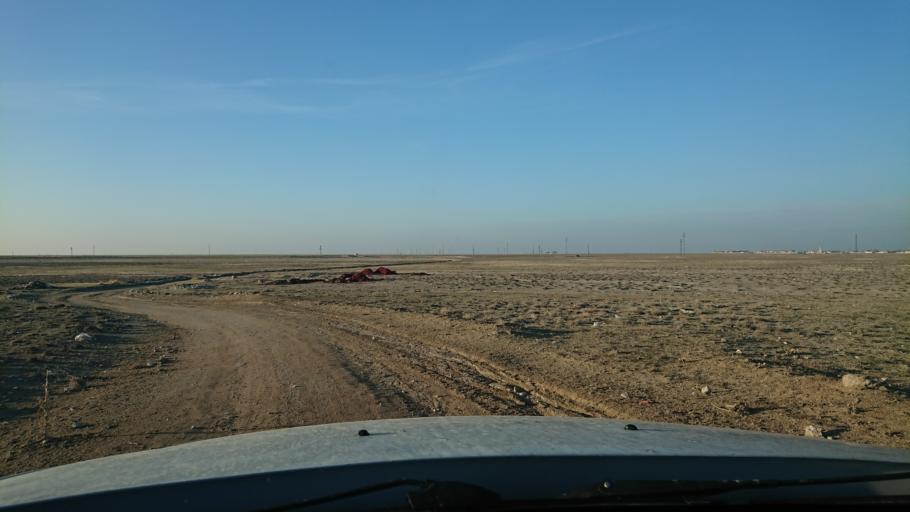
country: TR
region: Aksaray
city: Sultanhani
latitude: 38.2711
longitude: 33.5158
